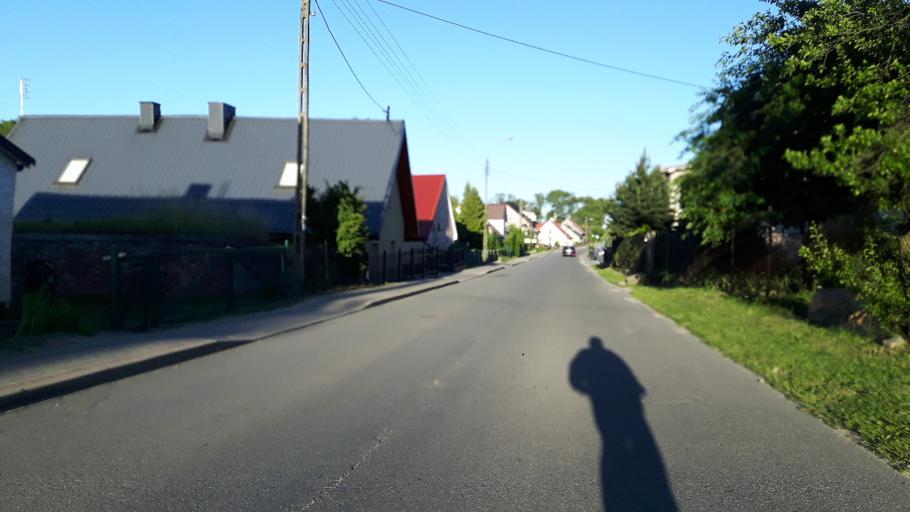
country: PL
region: Pomeranian Voivodeship
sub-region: Powiat pucki
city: Mosty
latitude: 54.6101
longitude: 18.5082
